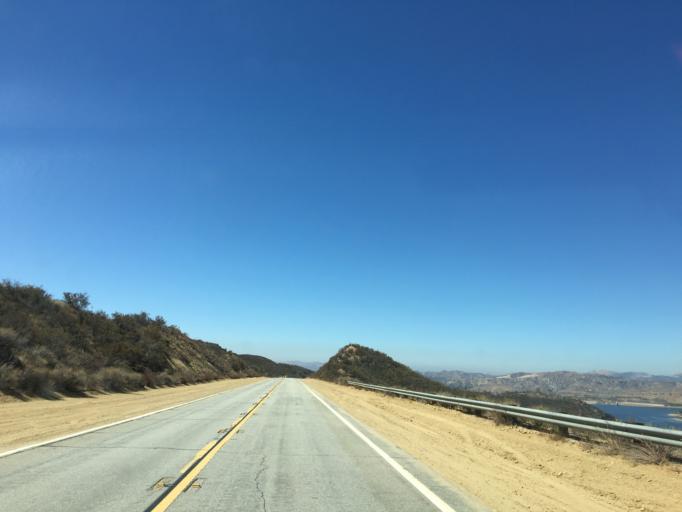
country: US
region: California
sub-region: Los Angeles County
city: Castaic
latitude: 34.5410
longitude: -118.5623
